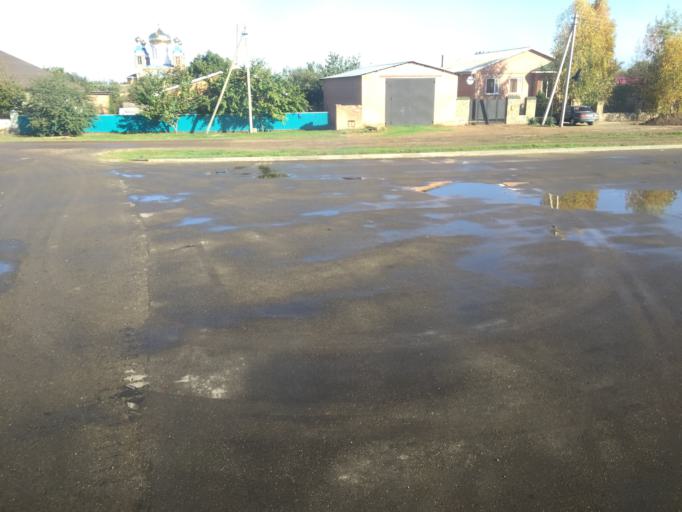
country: RU
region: Rostov
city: Peschanokopskoye
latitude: 46.1893
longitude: 41.0836
